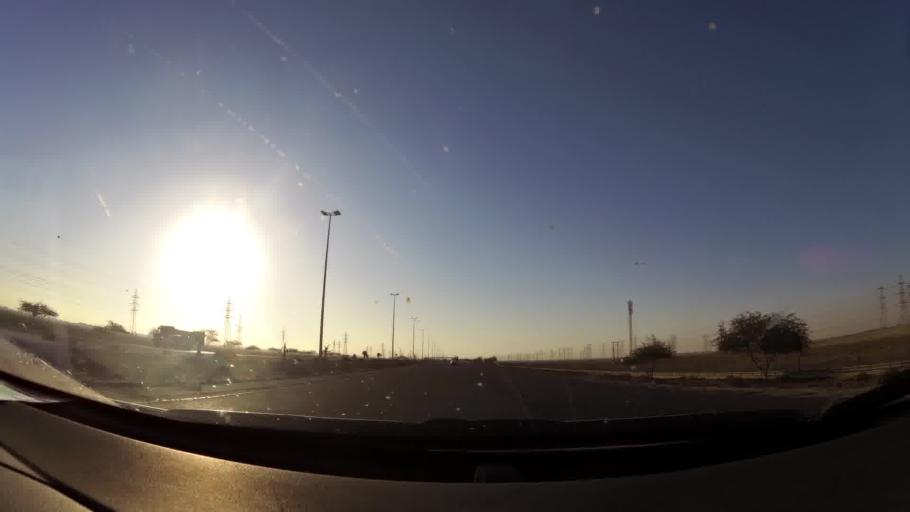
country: KW
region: Al Ahmadi
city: Al Fahahil
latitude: 28.8388
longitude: 48.2503
